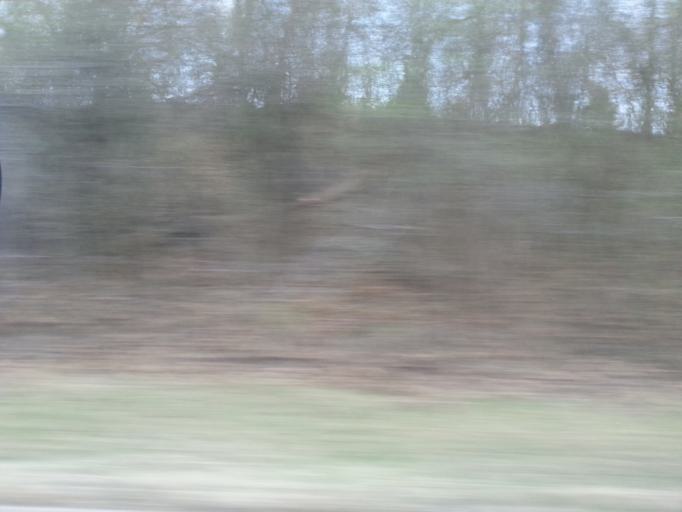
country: US
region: Minnesota
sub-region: Washington County
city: Afton
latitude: 44.8858
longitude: -92.7948
